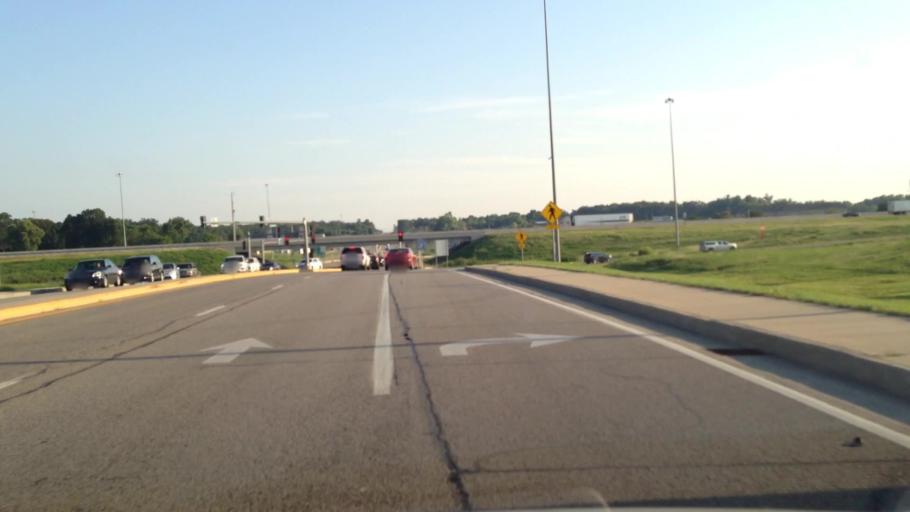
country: US
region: Missouri
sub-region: Jasper County
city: Duquesne
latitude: 37.0489
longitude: -94.4786
